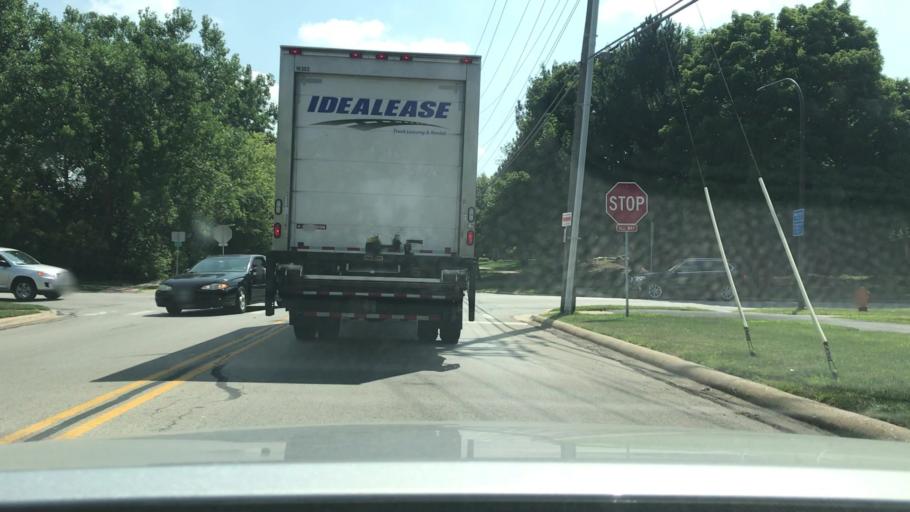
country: US
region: Illinois
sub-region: DuPage County
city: Naperville
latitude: 41.7404
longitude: -88.1234
